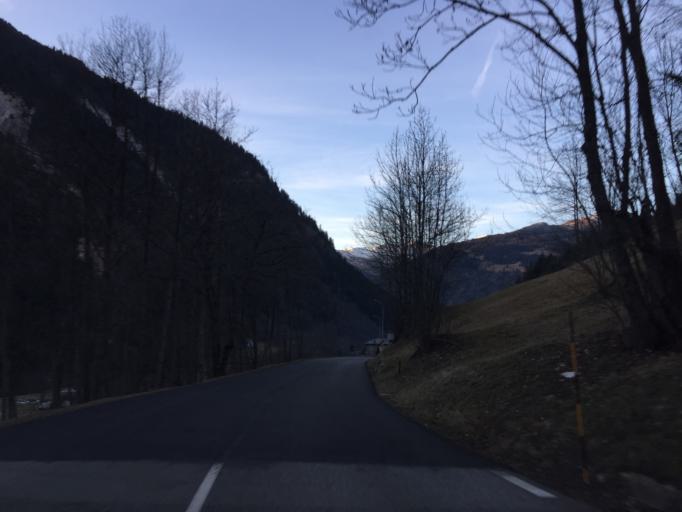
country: FR
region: Rhone-Alpes
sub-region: Departement de la Savoie
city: Bozel
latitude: 45.4205
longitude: 6.7019
